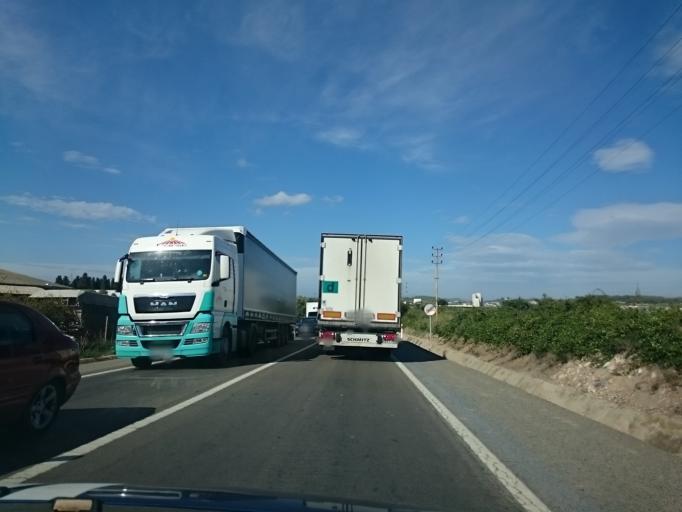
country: ES
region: Catalonia
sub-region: Provincia de Barcelona
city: Castellet
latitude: 41.2705
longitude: 1.6082
